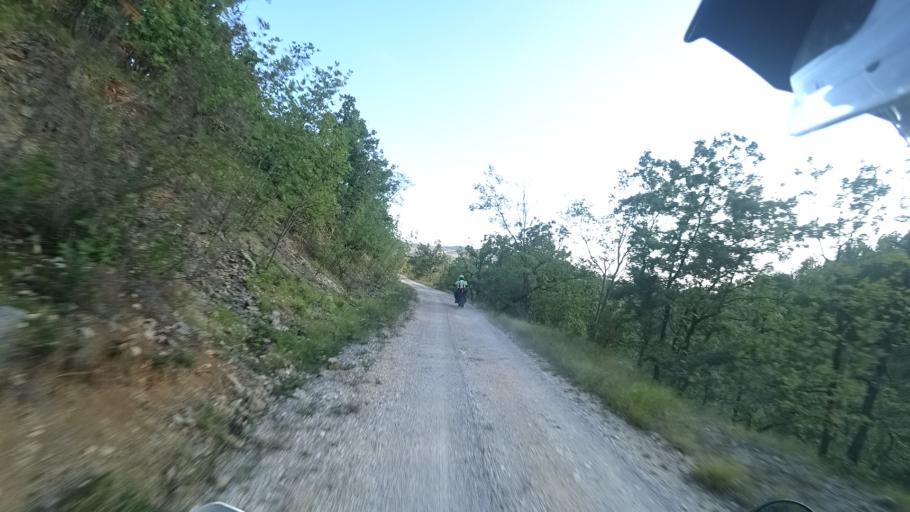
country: HR
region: Sibensko-Kniniska
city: Knin
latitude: 44.1378
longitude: 16.1279
